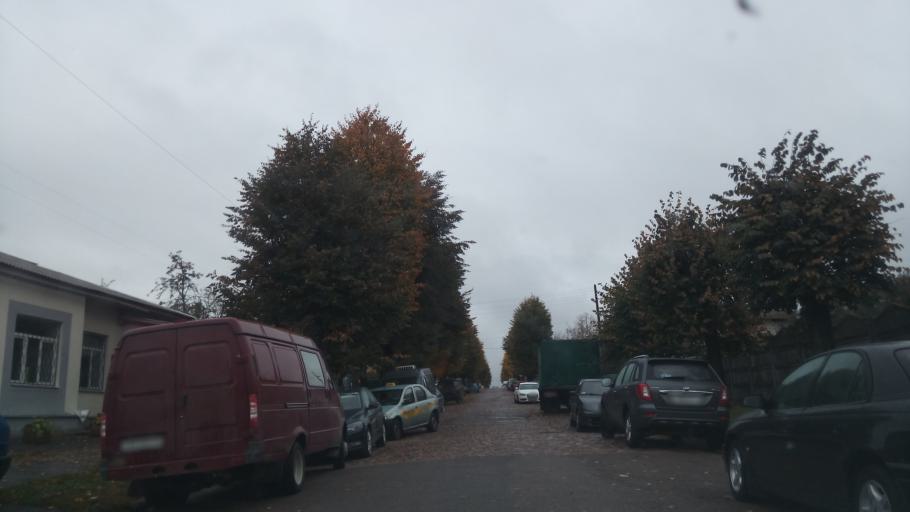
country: BY
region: Minsk
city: Minsk
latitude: 53.9439
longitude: 27.5960
